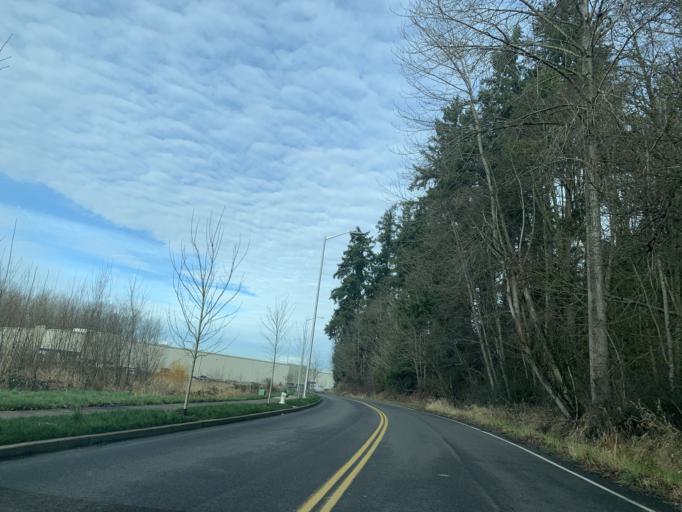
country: US
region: Washington
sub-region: Pierce County
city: Milton
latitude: 47.2298
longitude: -122.3216
